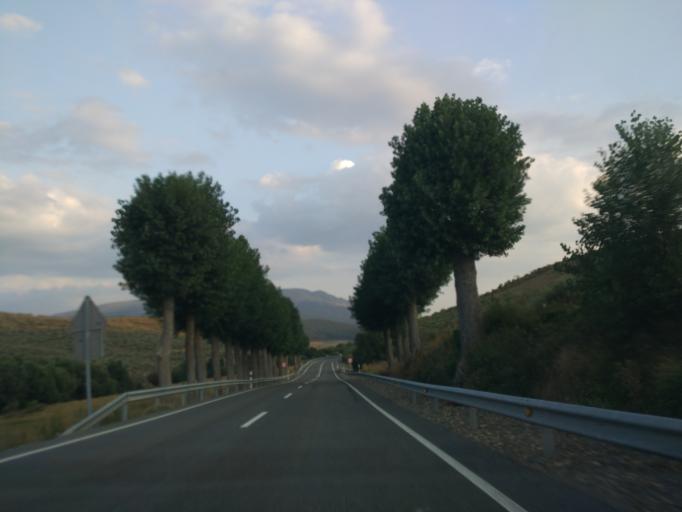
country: ES
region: Castille and Leon
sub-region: Provincia de Avila
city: San Martin del Pimpollar
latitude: 40.3868
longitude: -5.0209
